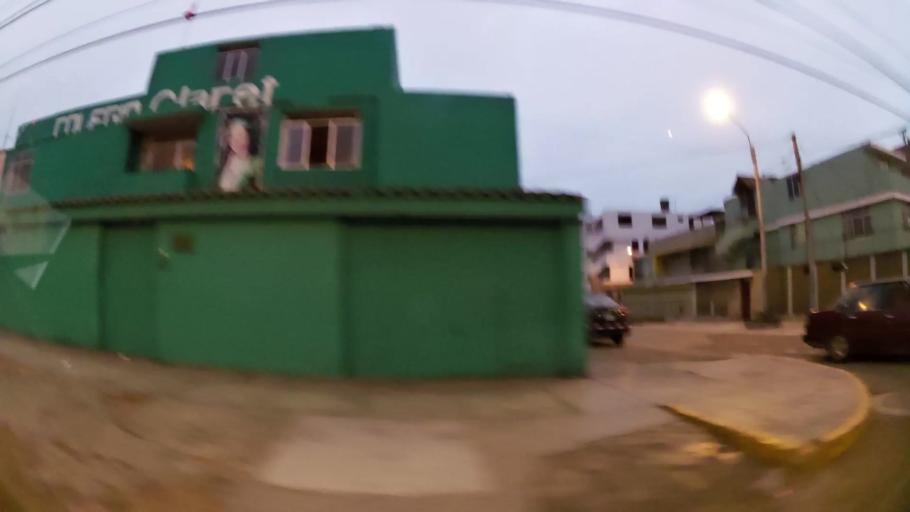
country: PE
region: Callao
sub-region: Callao
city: Callao
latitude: -12.0821
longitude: -77.0978
